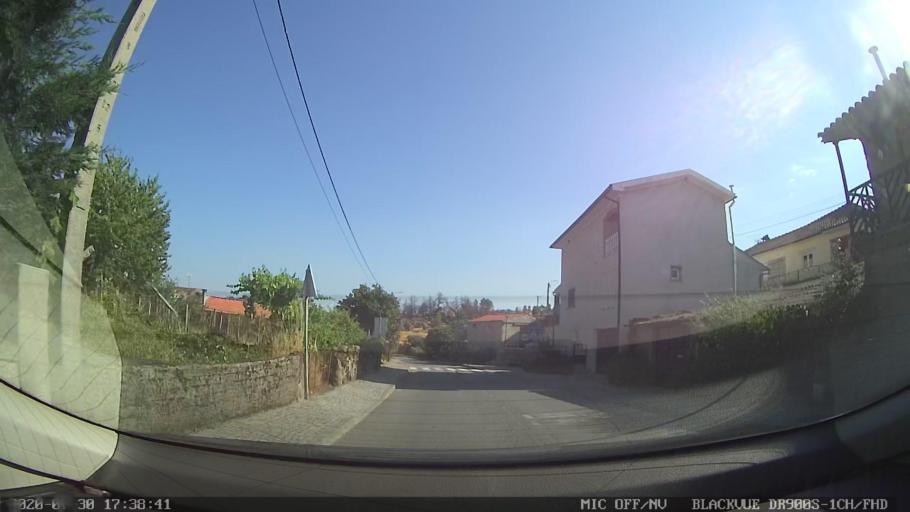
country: PT
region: Vila Real
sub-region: Murca
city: Murca
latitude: 41.3739
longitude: -7.5037
